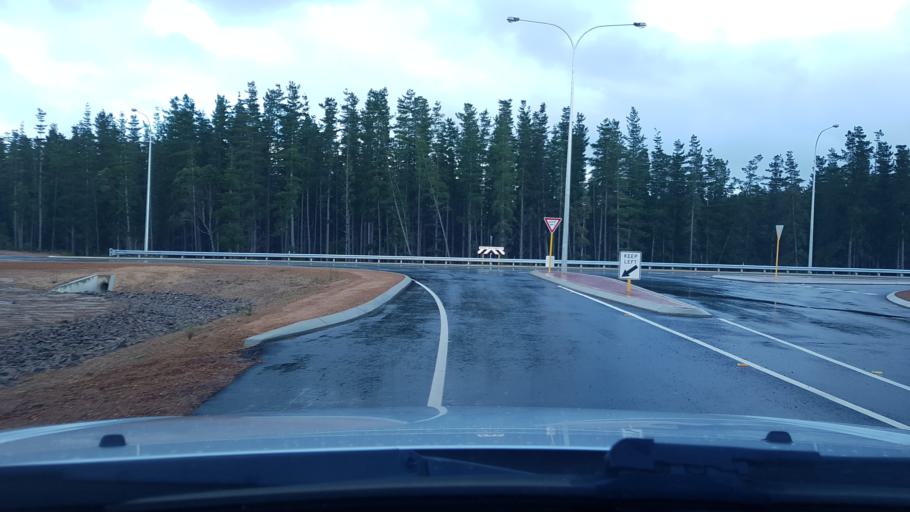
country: AU
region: Western Australia
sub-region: Augusta-Margaret River Shire
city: Margaret River
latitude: -33.9358
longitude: 115.0898
